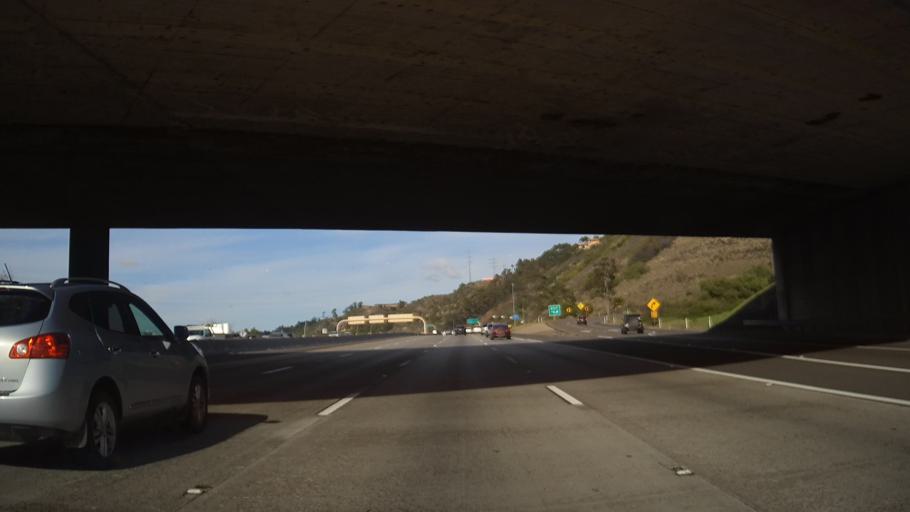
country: US
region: California
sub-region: San Diego County
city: San Diego
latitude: 32.7885
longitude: -117.1171
